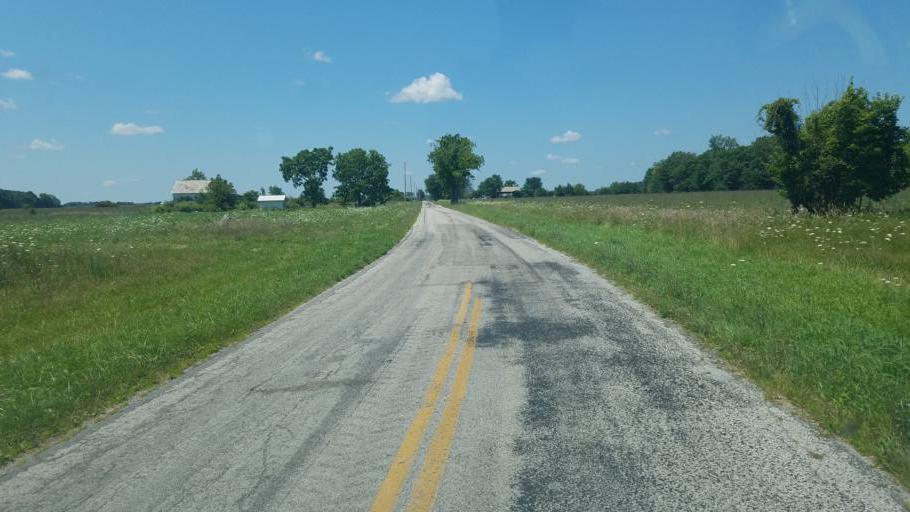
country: US
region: Ohio
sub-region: Union County
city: Richwood
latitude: 40.5628
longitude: -83.2750
